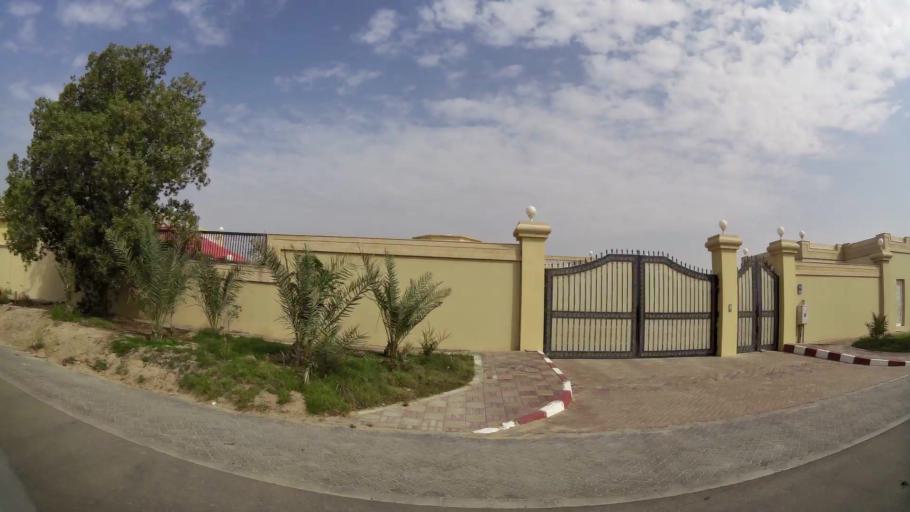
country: AE
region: Abu Dhabi
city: Abu Dhabi
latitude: 24.2741
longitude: 54.6644
